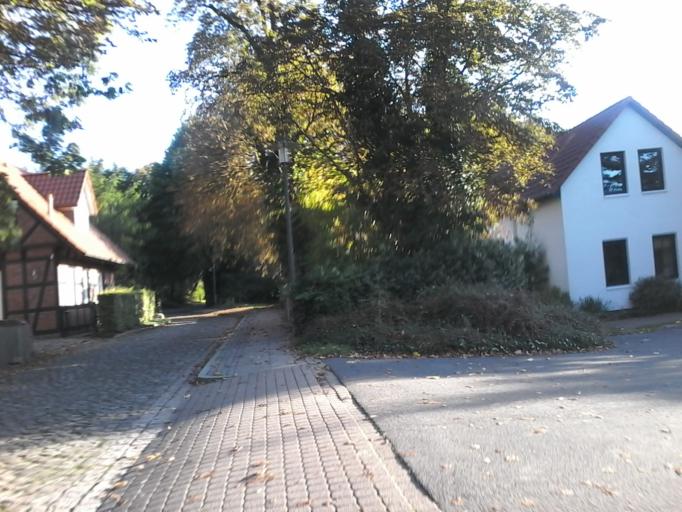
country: DE
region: Lower Saxony
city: Achim
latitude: 53.0051
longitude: 9.0373
